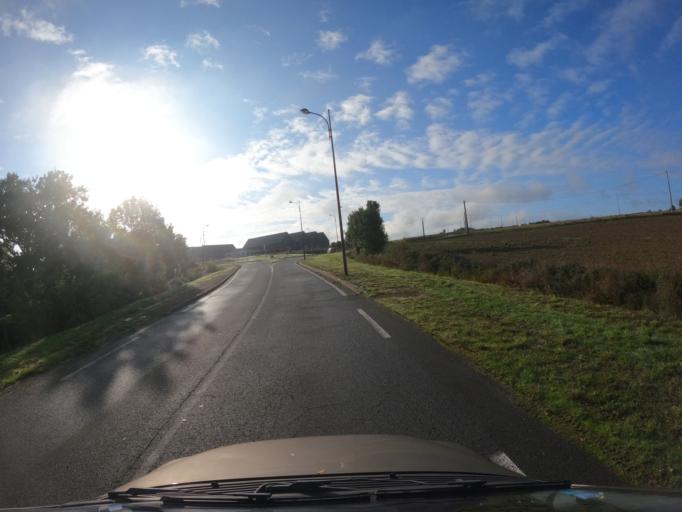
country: FR
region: Pays de la Loire
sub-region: Departement de Maine-et-Loire
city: La Seguiniere
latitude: 47.0568
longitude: -0.9451
